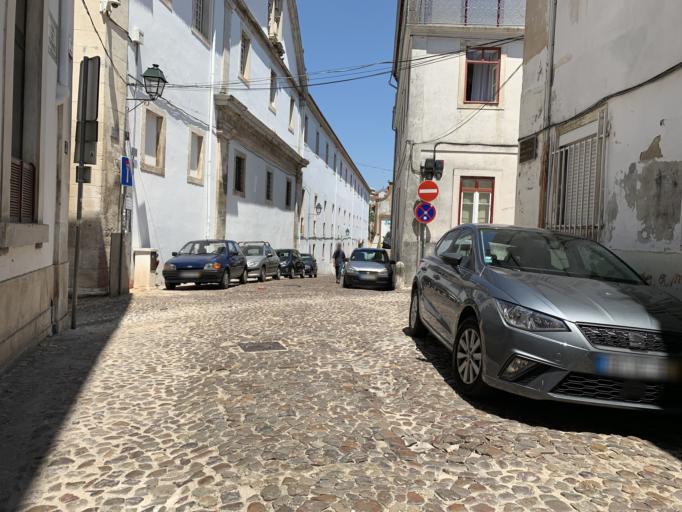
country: PT
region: Coimbra
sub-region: Coimbra
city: Coimbra
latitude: 40.2098
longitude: -8.4278
